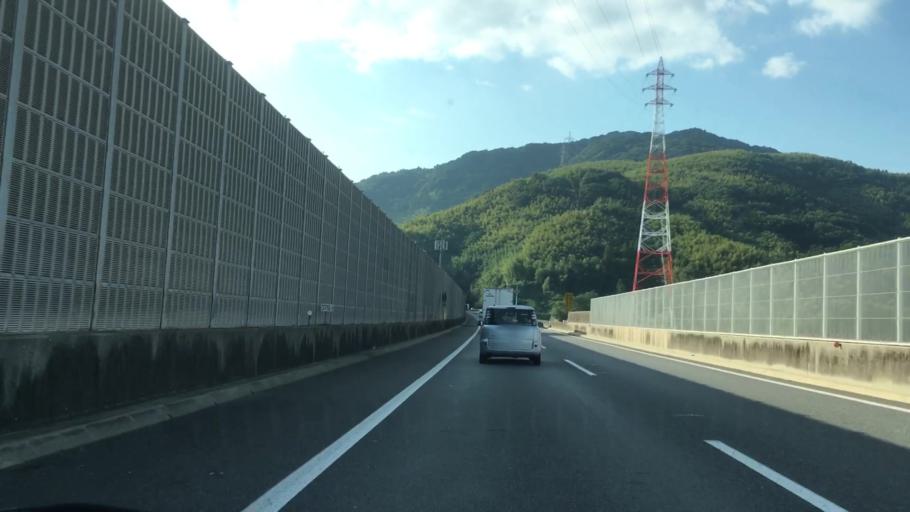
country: JP
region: Yamaguchi
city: Tokuyama
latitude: 34.0866
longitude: 131.7808
